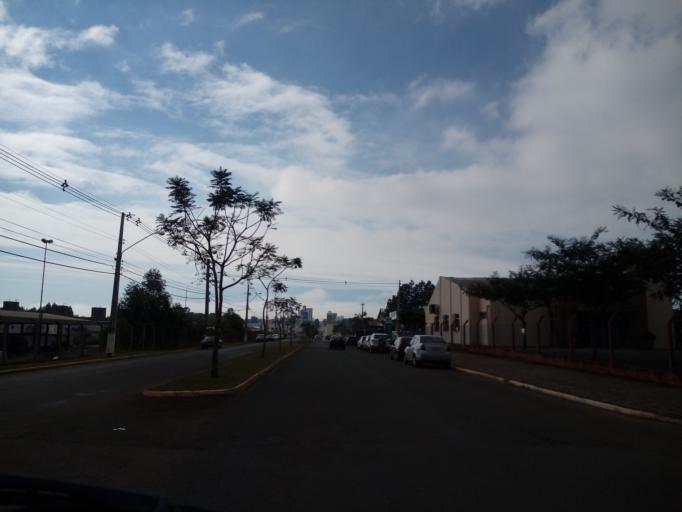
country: BR
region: Santa Catarina
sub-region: Chapeco
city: Chapeco
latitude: -27.0910
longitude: -52.5973
